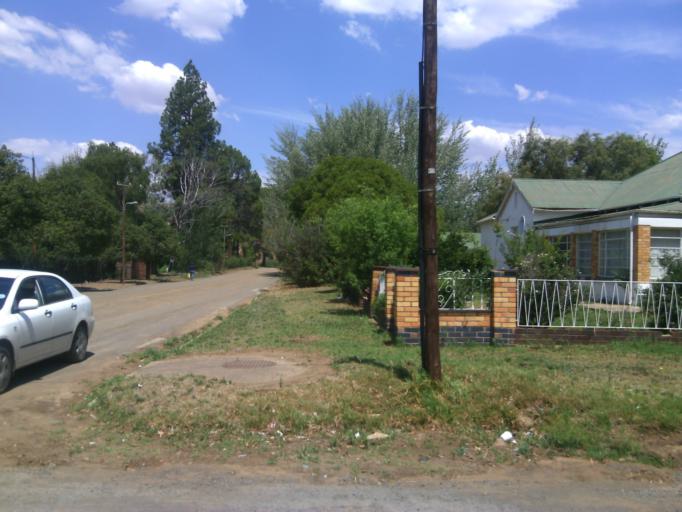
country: ZA
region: Orange Free State
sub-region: Xhariep District Municipality
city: Dewetsdorp
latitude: -29.5857
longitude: 26.6649
